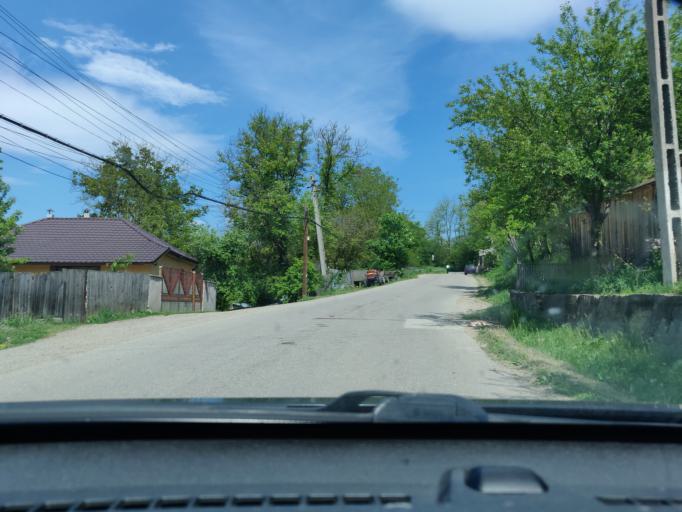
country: RO
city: Vizantea-Manastireasca
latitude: 45.9555
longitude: 26.8310
